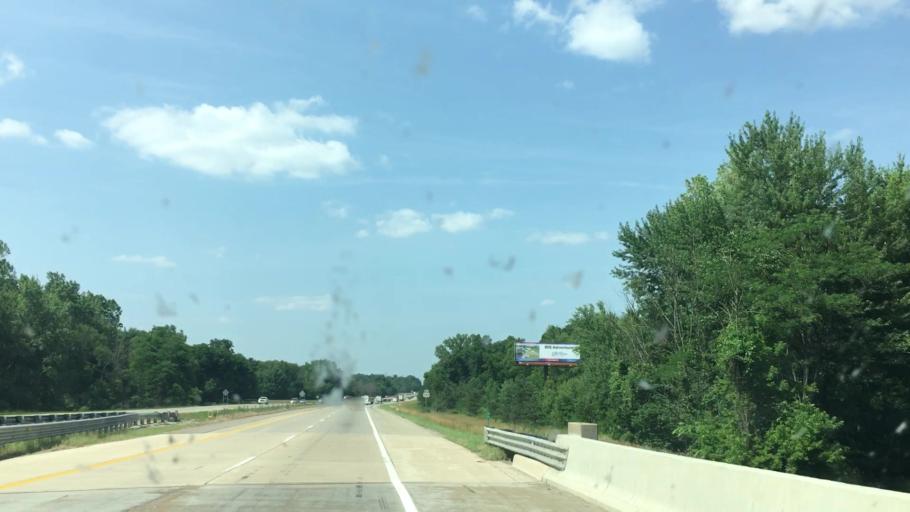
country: US
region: Michigan
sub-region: Allegan County
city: Plainwell
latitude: 42.4684
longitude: -85.6528
